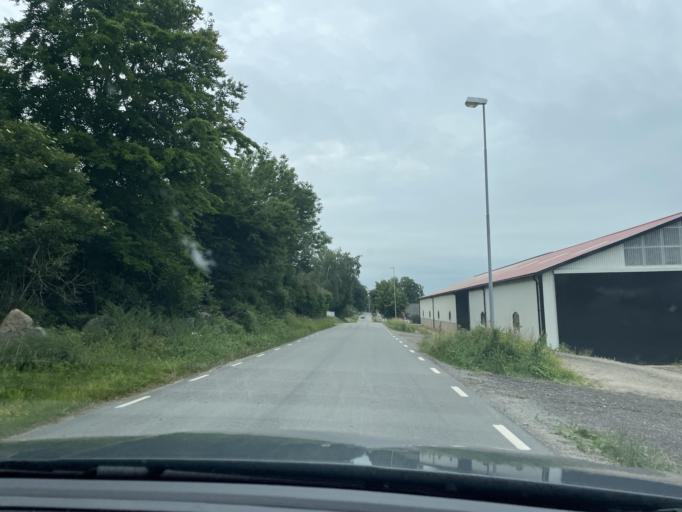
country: SE
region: Blekinge
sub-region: Solvesborgs Kommun
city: Soelvesborg
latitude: 56.0301
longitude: 14.6358
